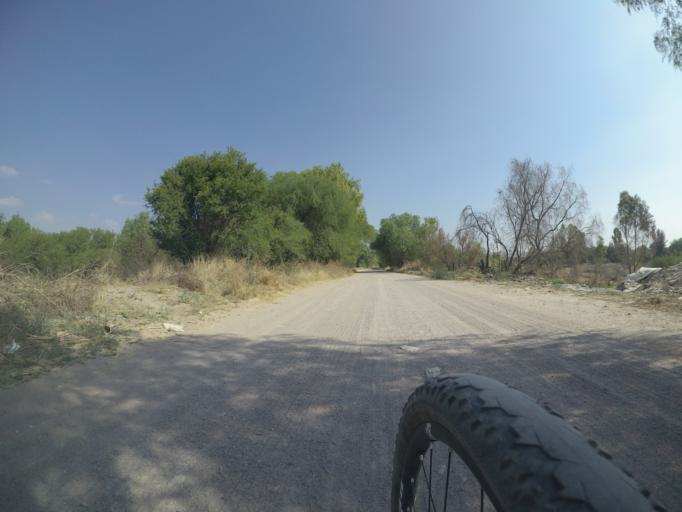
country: MX
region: Aguascalientes
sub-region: Jesus Maria
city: Paseos de las Haciendas [Fraccionamiento]
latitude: 21.9983
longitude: -102.3355
